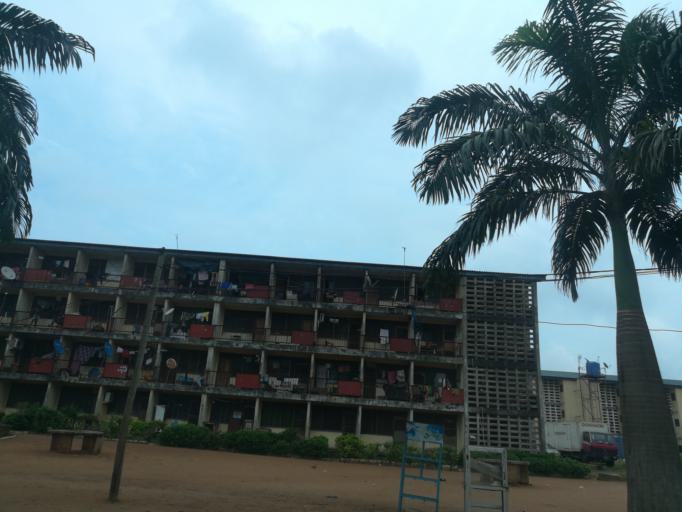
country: NG
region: Lagos
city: Oshodi
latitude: 6.5688
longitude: 3.3557
